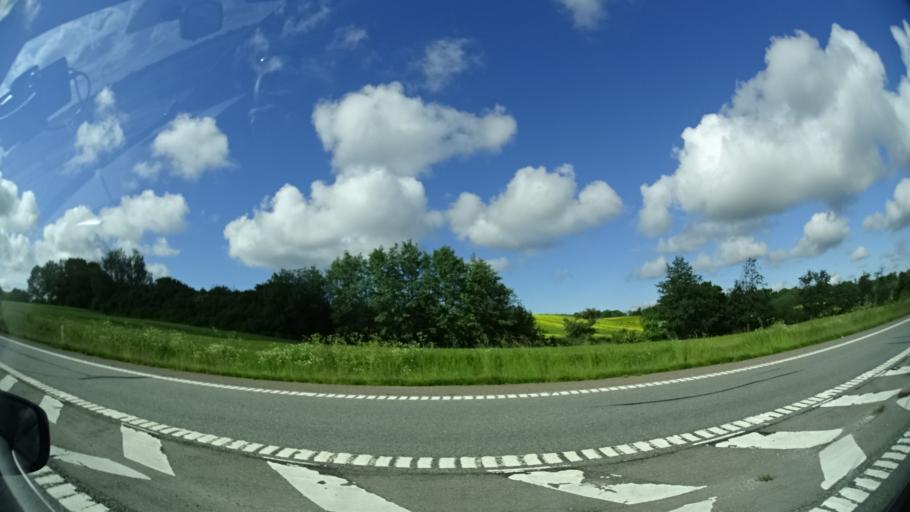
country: DK
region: Central Jutland
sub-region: Syddjurs Kommune
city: Ronde
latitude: 56.3007
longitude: 10.5100
